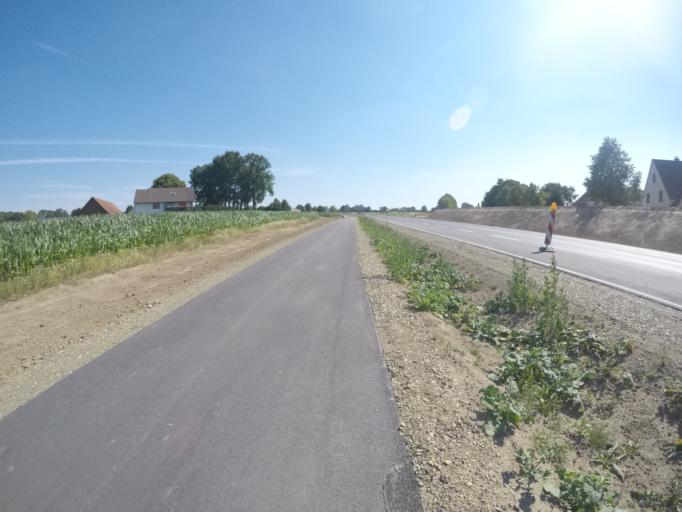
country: DE
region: North Rhine-Westphalia
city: Loehne
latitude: 52.1761
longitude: 8.7500
